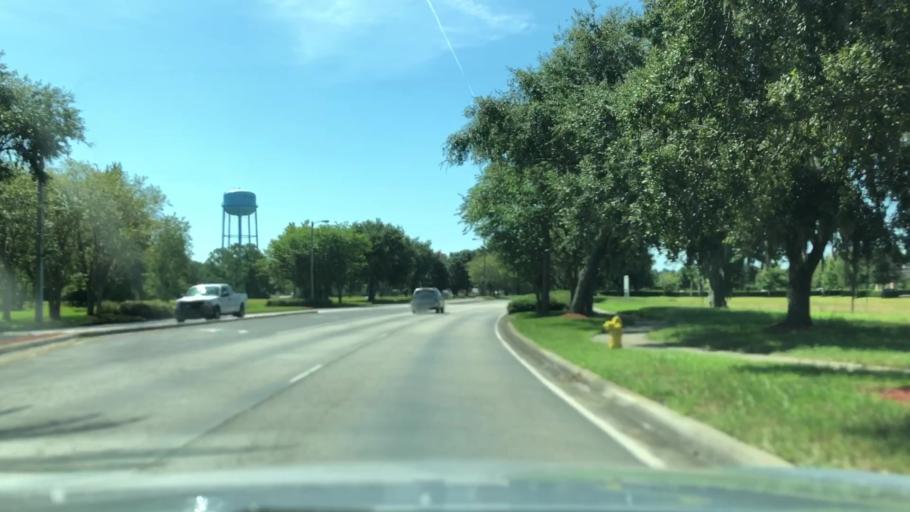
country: US
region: Florida
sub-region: Saint Johns County
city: Saint Augustine
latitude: 29.9215
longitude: -81.4102
